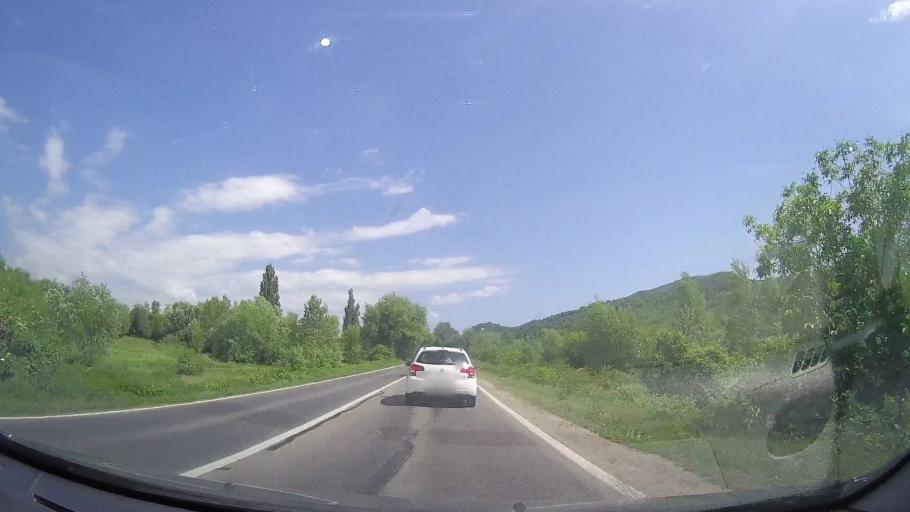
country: RO
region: Prahova
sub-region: Comuna Gura Vitioarei
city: Fagetu
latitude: 45.1331
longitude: 26.0300
